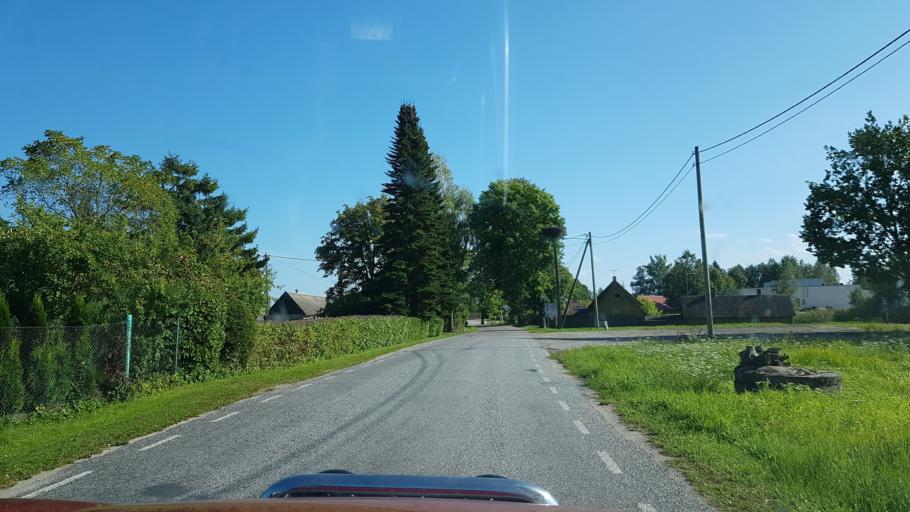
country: EE
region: Polvamaa
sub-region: Raepina vald
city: Rapina
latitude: 58.2371
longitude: 27.4686
